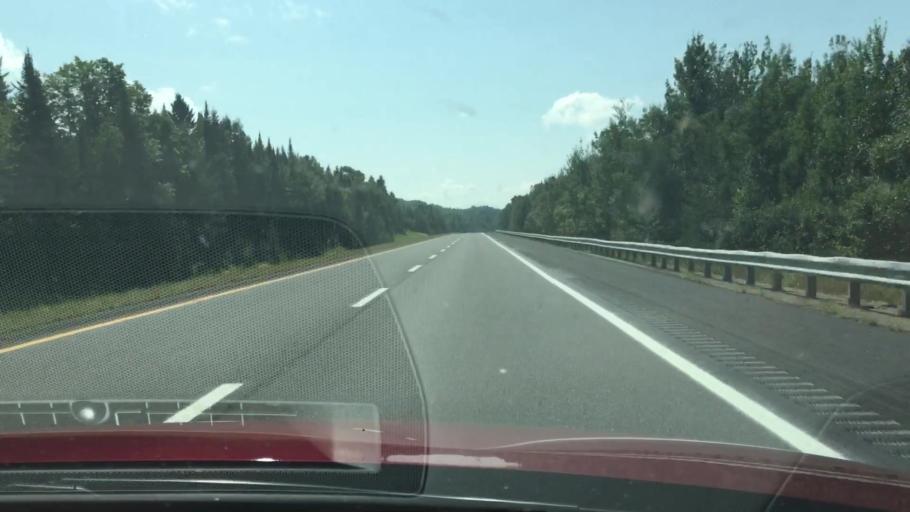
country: US
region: Maine
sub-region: Penobscot County
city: Patten
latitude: 45.9257
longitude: -68.3658
